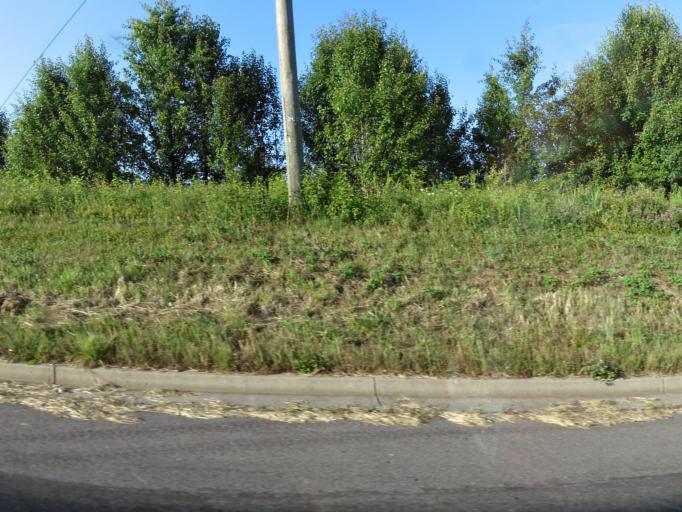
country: US
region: Tennessee
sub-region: Sevier County
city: Seymour
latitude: 35.8634
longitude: -83.7452
